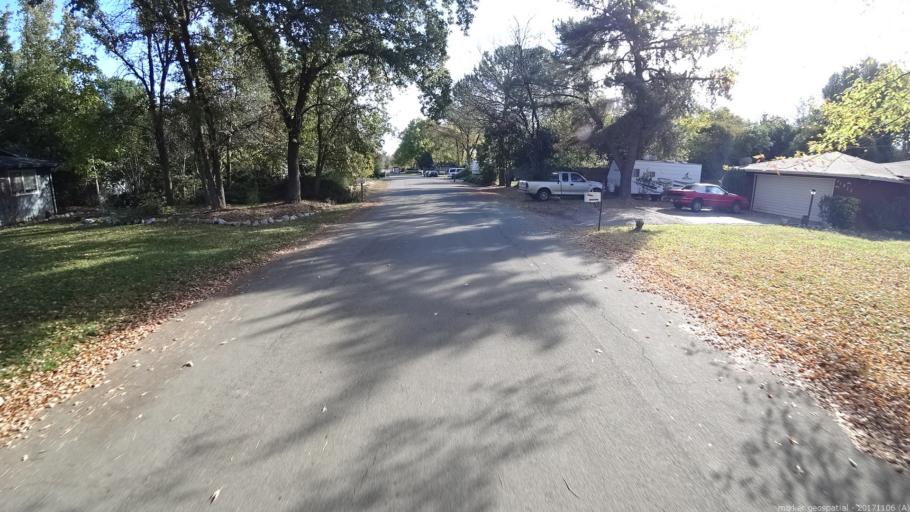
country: US
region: California
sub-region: Shasta County
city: Palo Cedro
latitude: 40.5416
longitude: -122.2411
